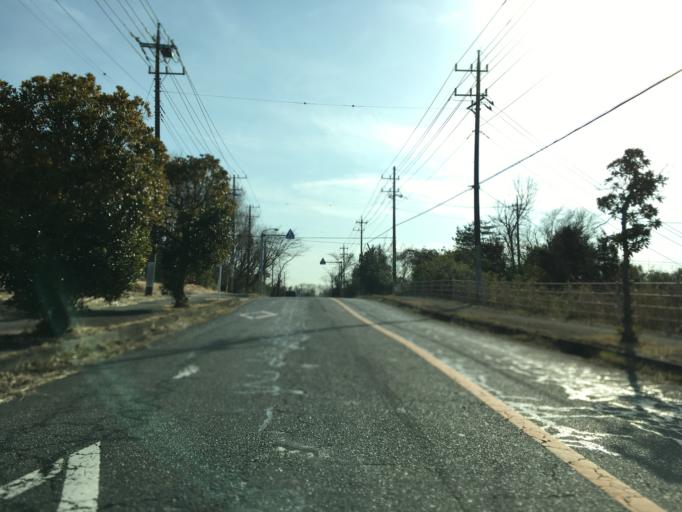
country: JP
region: Ibaraki
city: Takahagi
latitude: 36.7527
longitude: 140.7063
